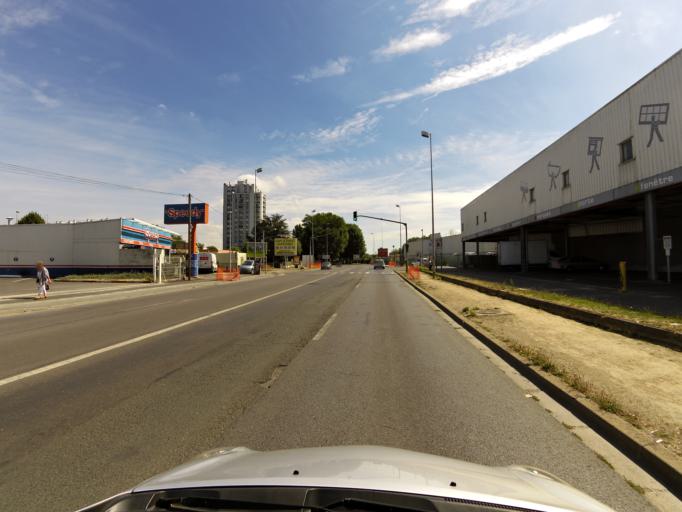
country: FR
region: Ile-de-France
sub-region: Departement de Seine-Saint-Denis
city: Noisy-le-Grand
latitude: 48.8657
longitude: 2.5665
